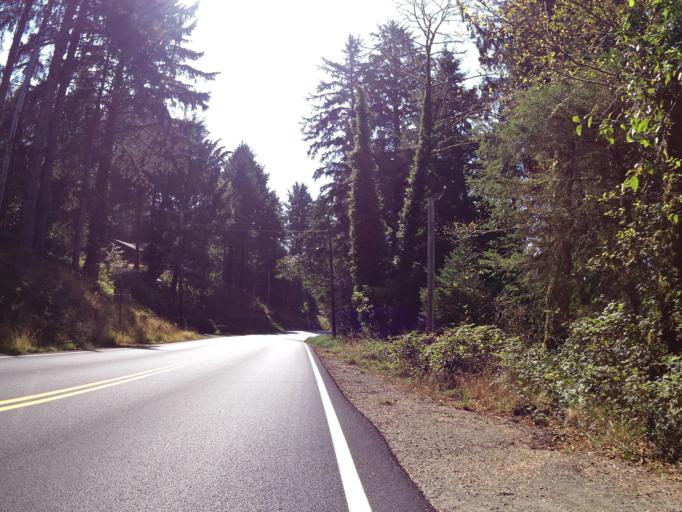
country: US
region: Oregon
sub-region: Tillamook County
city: Pacific City
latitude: 45.2701
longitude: -123.9469
